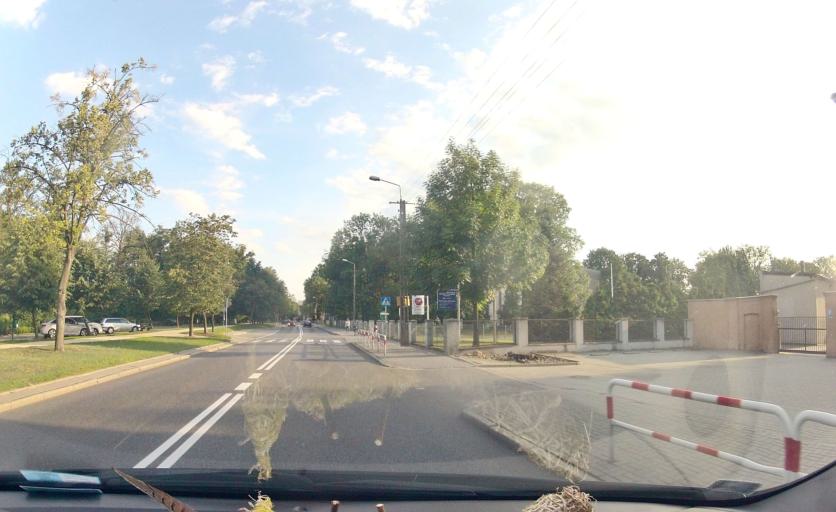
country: PL
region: Opole Voivodeship
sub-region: Powiat kluczborski
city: Kluczbork
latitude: 50.9699
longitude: 18.2178
